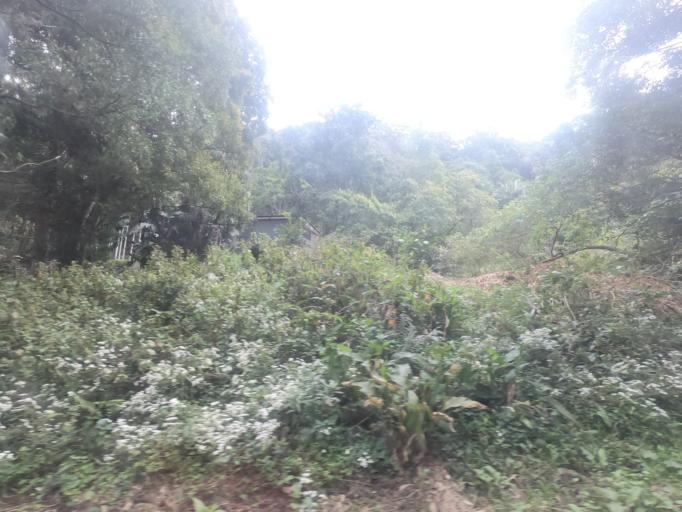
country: AU
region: New South Wales
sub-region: Wollongong
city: Bulli
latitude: -34.2891
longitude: 150.9382
